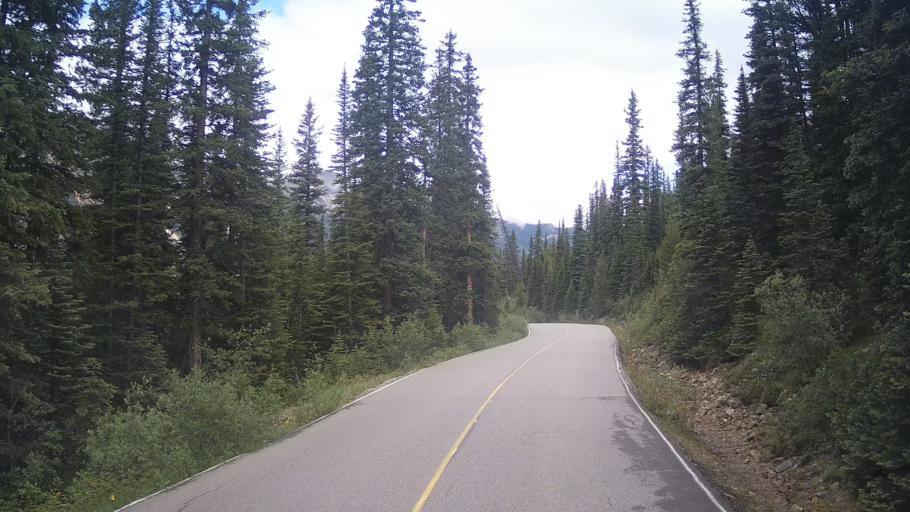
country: CA
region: Alberta
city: Jasper Park Lodge
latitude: 52.6983
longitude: -118.0585
